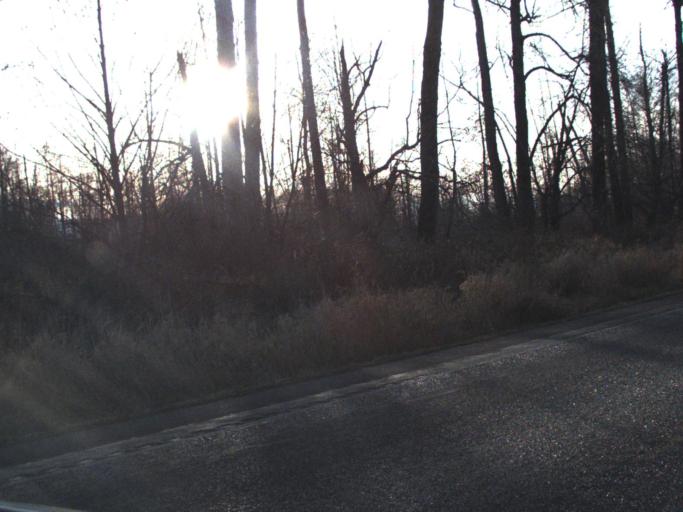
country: US
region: Washington
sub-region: Skagit County
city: Sedro-Woolley
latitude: 48.5284
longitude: -122.1657
